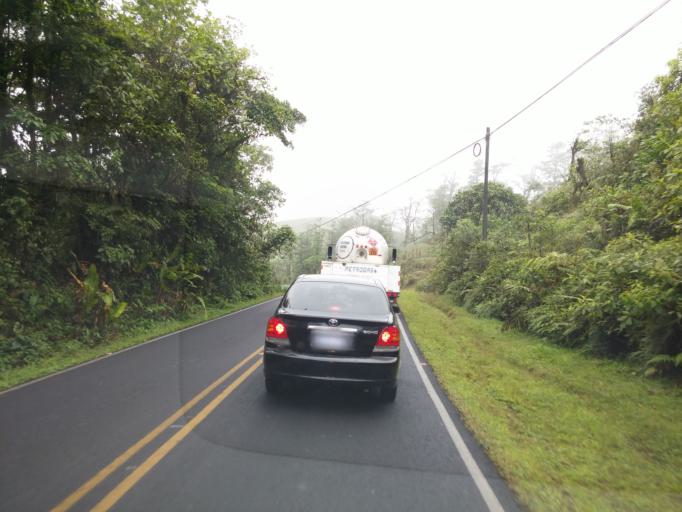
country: CR
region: Alajuela
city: San Ramon
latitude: 10.1860
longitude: -84.5051
